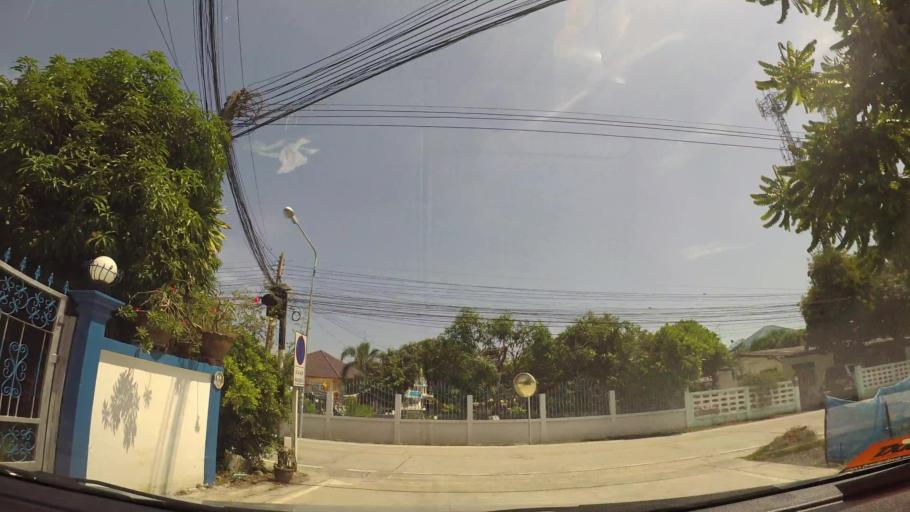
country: TH
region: Chon Buri
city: Chon Buri
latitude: 13.3207
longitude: 100.9540
